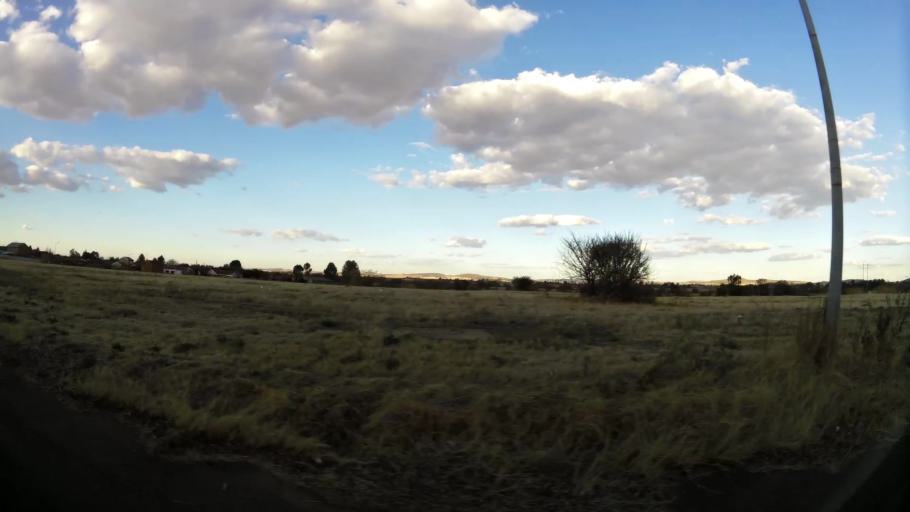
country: ZA
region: North-West
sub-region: Dr Kenneth Kaunda District Municipality
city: Potchefstroom
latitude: -26.7443
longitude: 27.0970
